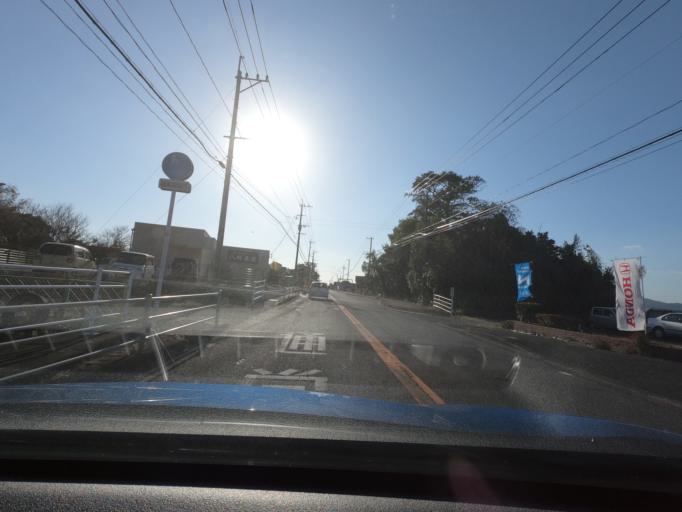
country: JP
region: Kagoshima
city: Izumi
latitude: 32.1057
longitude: 130.3184
